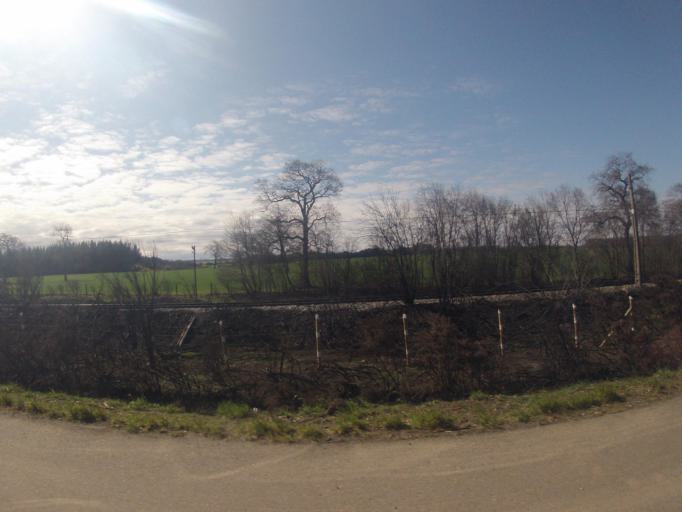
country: CL
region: Araucania
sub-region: Provincia de Malleco
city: Victoria
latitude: -38.1537
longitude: -72.3067
